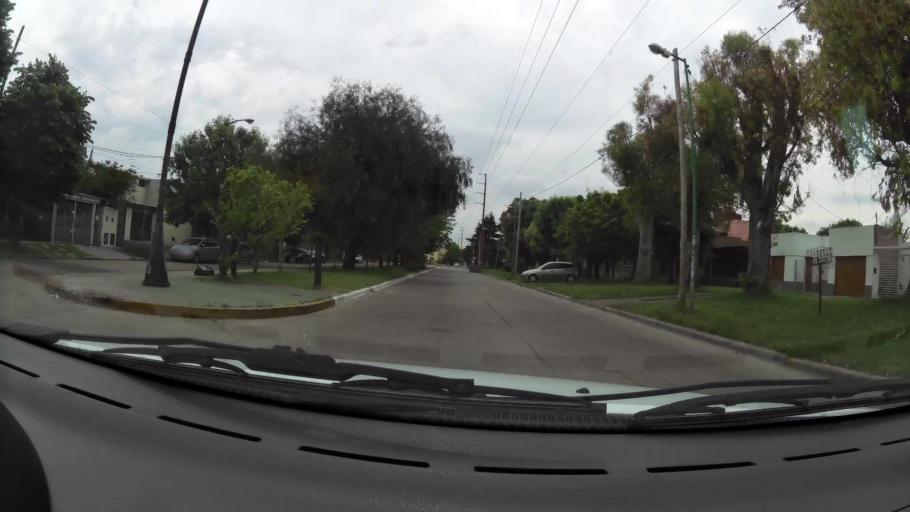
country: AR
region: Buenos Aires
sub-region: Partido de La Plata
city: La Plata
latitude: -34.9039
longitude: -57.9849
